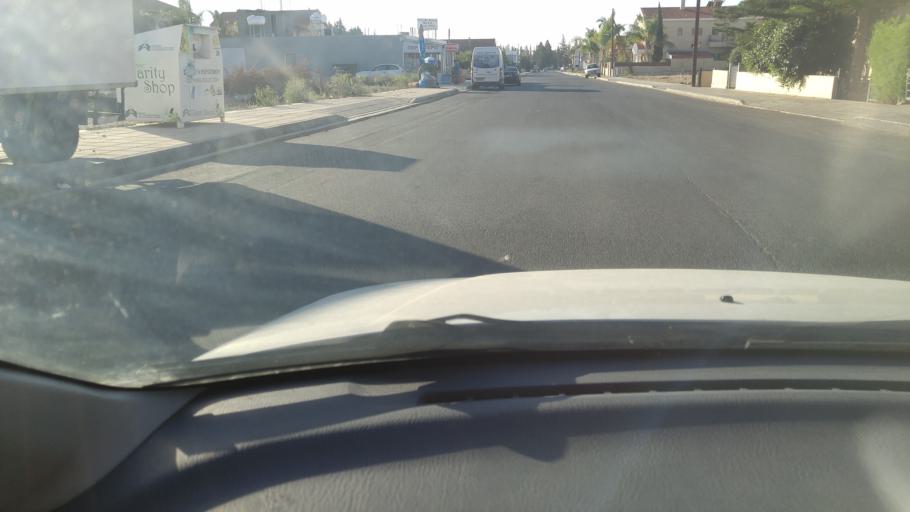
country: CY
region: Limassol
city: Ypsonas
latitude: 34.6572
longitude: 32.9732
